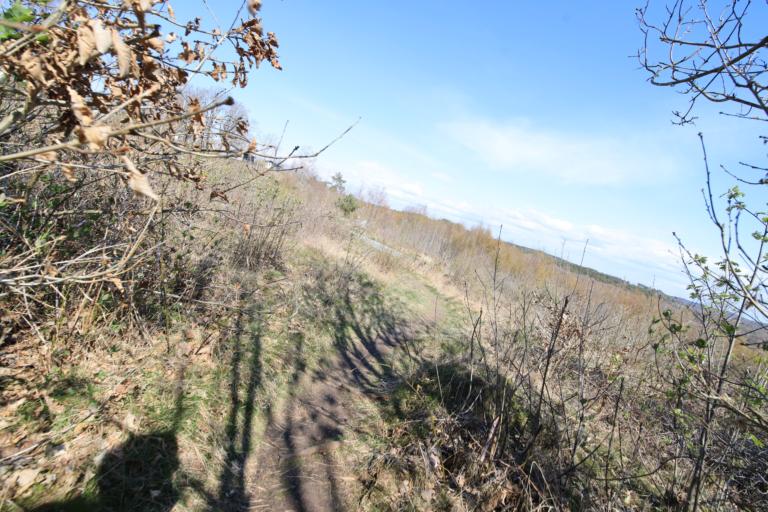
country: SE
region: Halland
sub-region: Varbergs Kommun
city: Varberg
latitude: 57.1791
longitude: 12.2435
